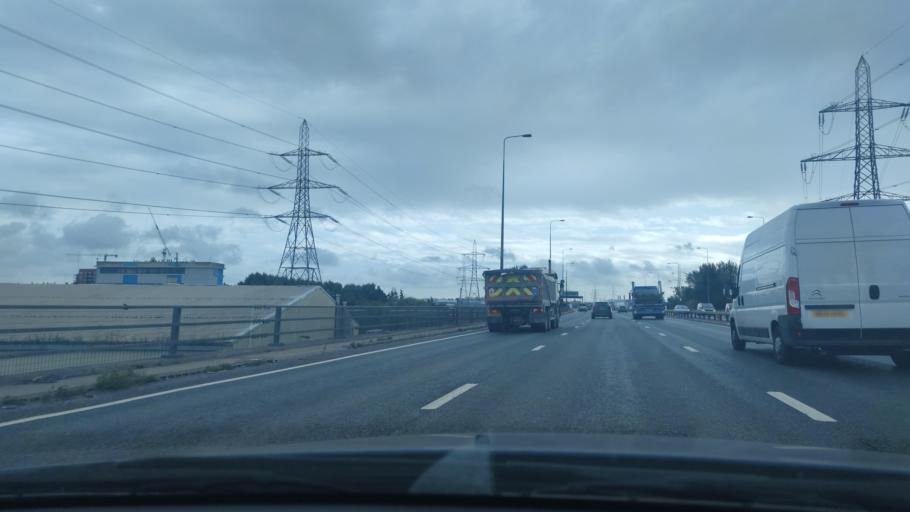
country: GB
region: England
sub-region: Greater London
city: Dagenham
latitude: 51.5226
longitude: 0.1586
